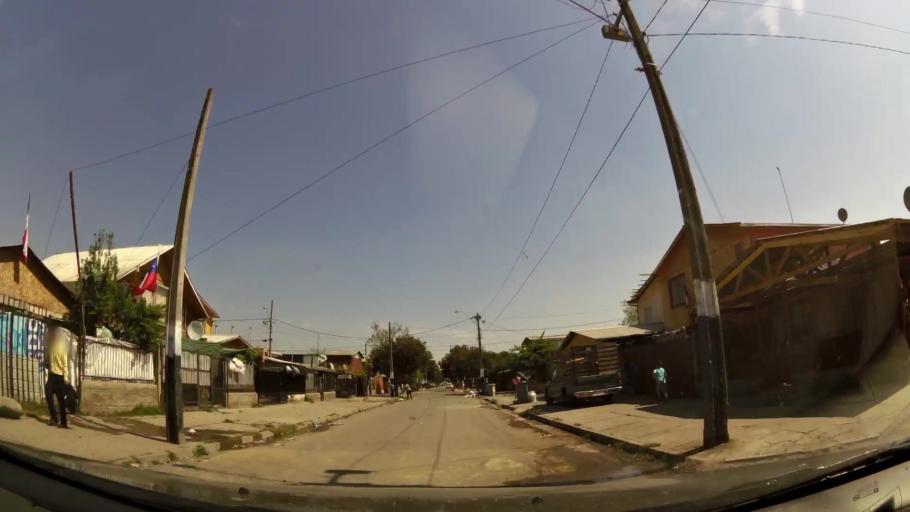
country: CL
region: Santiago Metropolitan
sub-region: Provincia de Santiago
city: La Pintana
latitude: -33.5919
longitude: -70.6151
